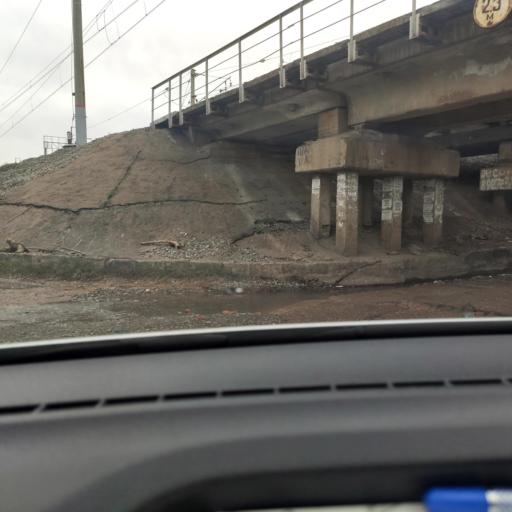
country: RU
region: Bashkortostan
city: Avdon
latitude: 54.6220
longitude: 55.5994
